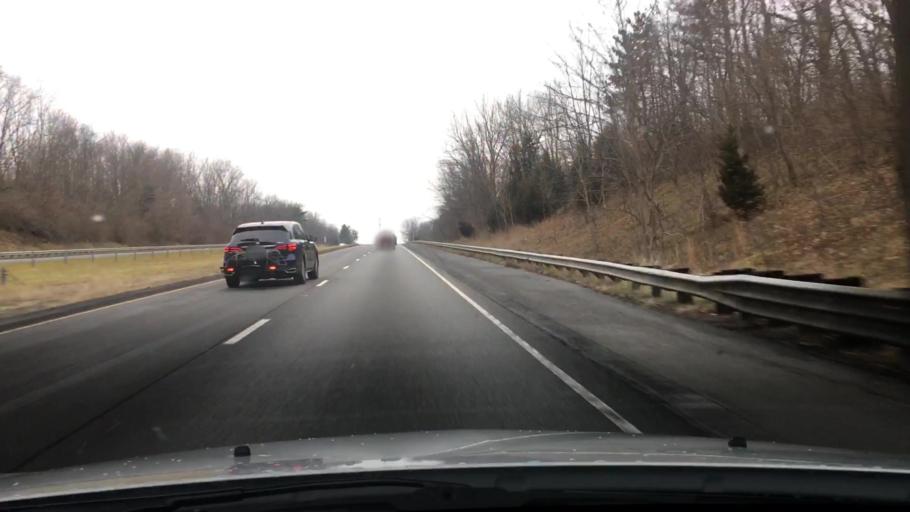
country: US
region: Indiana
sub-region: Boone County
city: Zionsville
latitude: 39.9105
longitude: -86.3210
